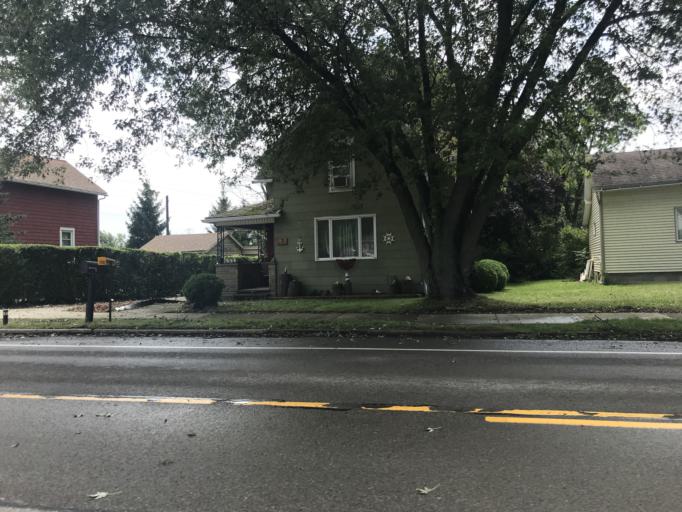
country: US
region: New York
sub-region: Chautauqua County
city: Dunkirk
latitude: 42.4848
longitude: -79.3519
